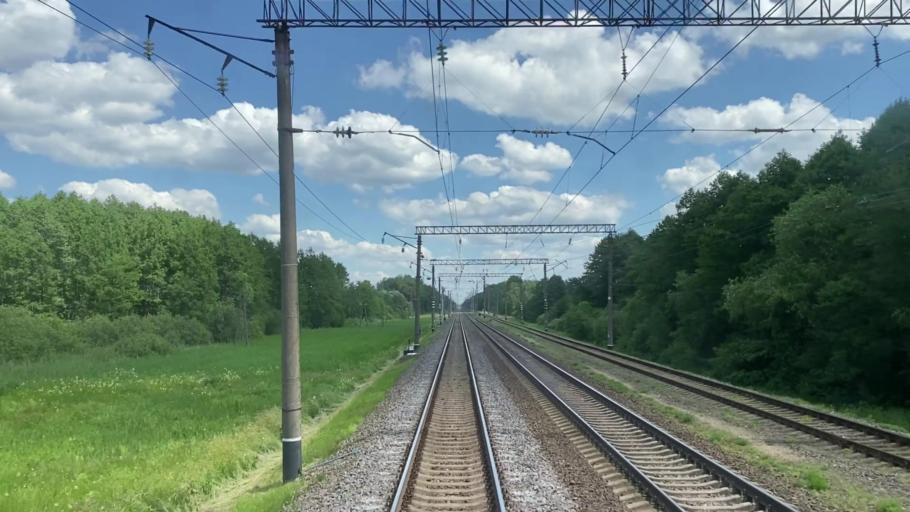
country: BY
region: Brest
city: Byaroza
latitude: 52.5384
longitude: 24.9258
